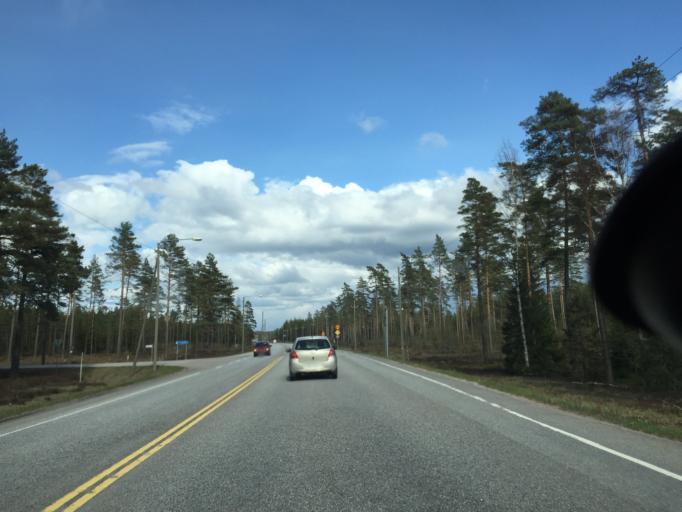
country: FI
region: Uusimaa
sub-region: Raaseporin
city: Pohja
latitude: 60.0087
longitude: 23.5443
